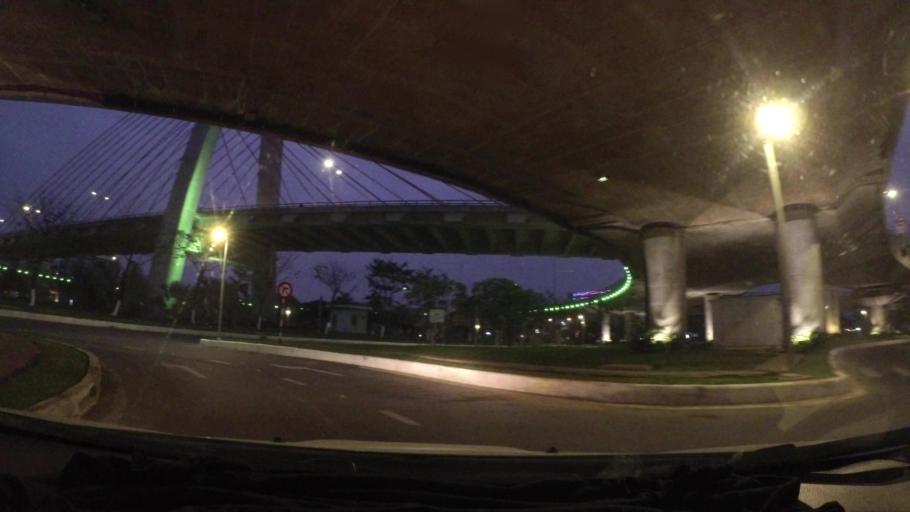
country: VN
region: Da Nang
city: Thanh Khe
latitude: 16.0622
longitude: 108.1781
